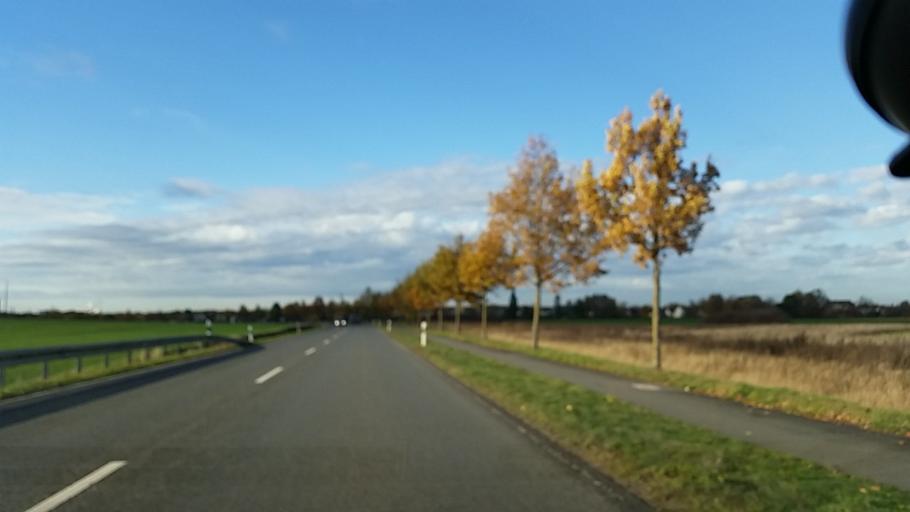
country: DE
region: Lower Saxony
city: Danndorf
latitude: 52.4242
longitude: 10.8569
